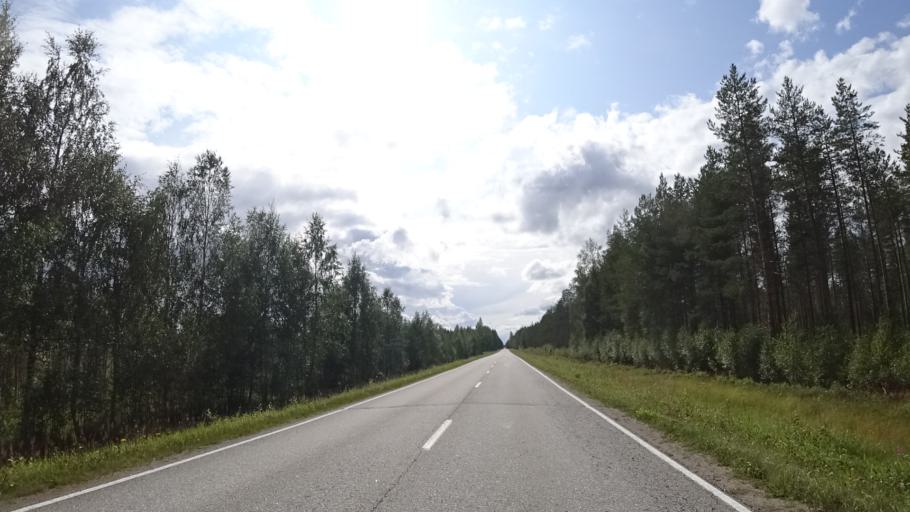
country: FI
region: North Karelia
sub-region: Joensuu
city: Ilomantsi
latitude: 62.7647
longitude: 31.0280
